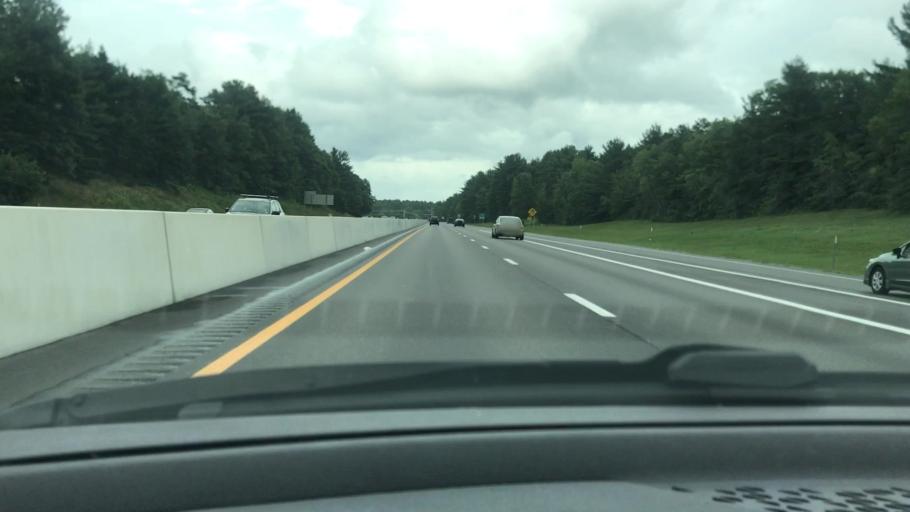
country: US
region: New Hampshire
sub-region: Merrimack County
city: Concord
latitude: 43.2252
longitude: -71.5035
